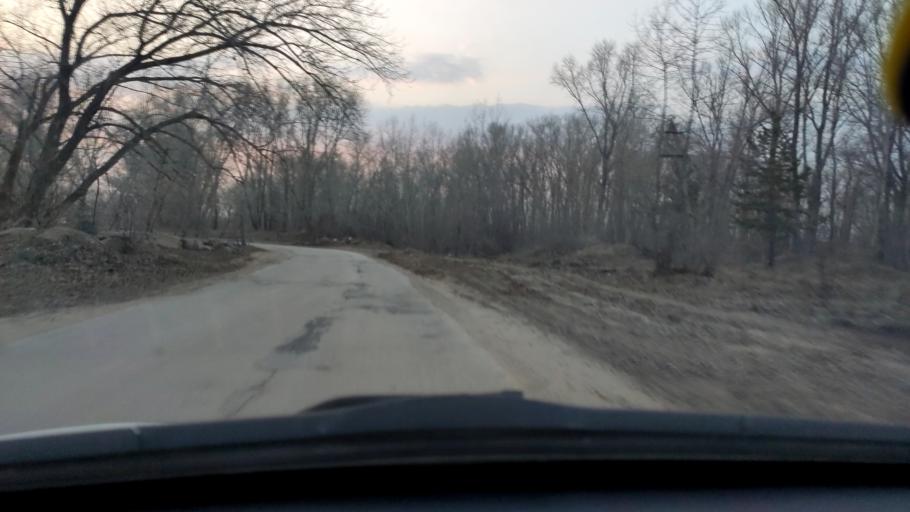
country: RU
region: Samara
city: Zhigulevsk
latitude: 53.4583
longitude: 49.5125
